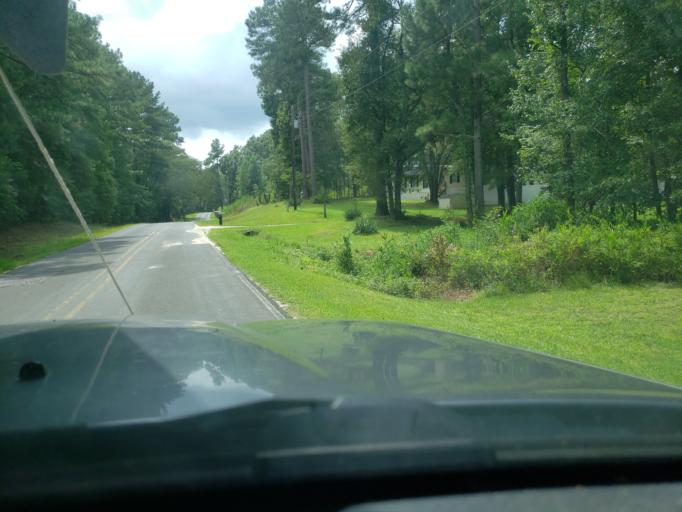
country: US
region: North Carolina
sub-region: Wake County
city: Zebulon
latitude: 35.8977
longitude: -78.3343
